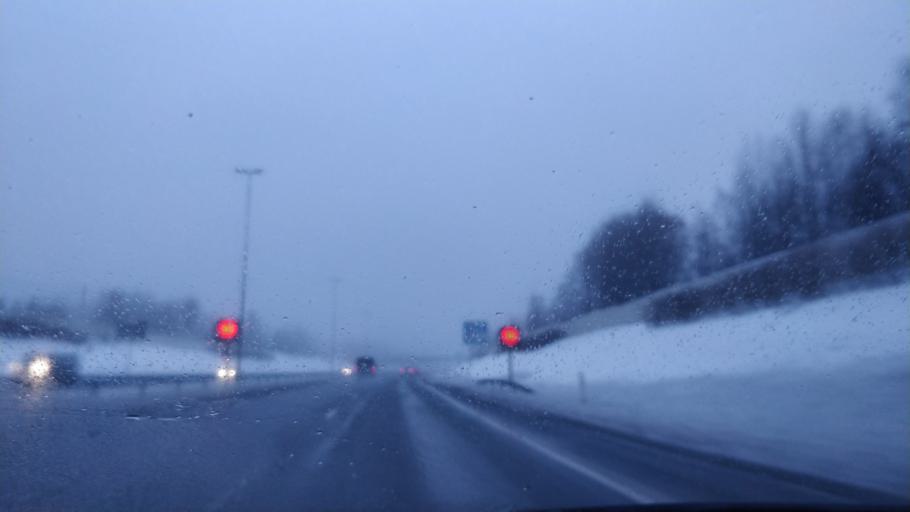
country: FI
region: Lapland
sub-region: Kemi-Tornio
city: Kemi
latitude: 65.7476
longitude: 24.5783
